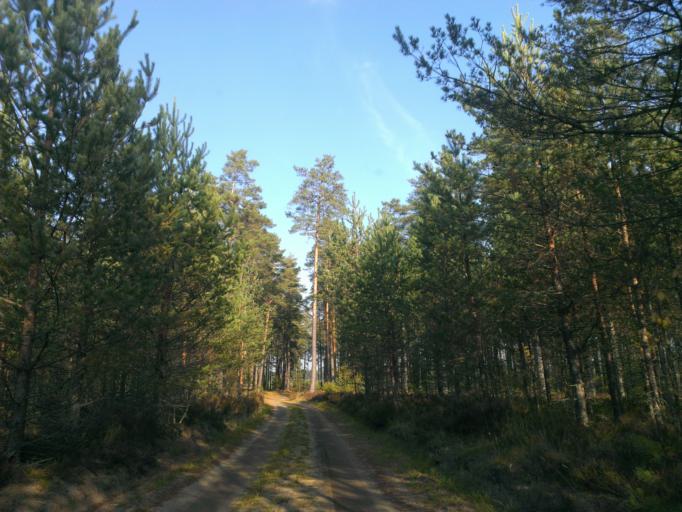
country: LV
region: Garkalne
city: Garkalne
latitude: 57.0195
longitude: 24.4826
